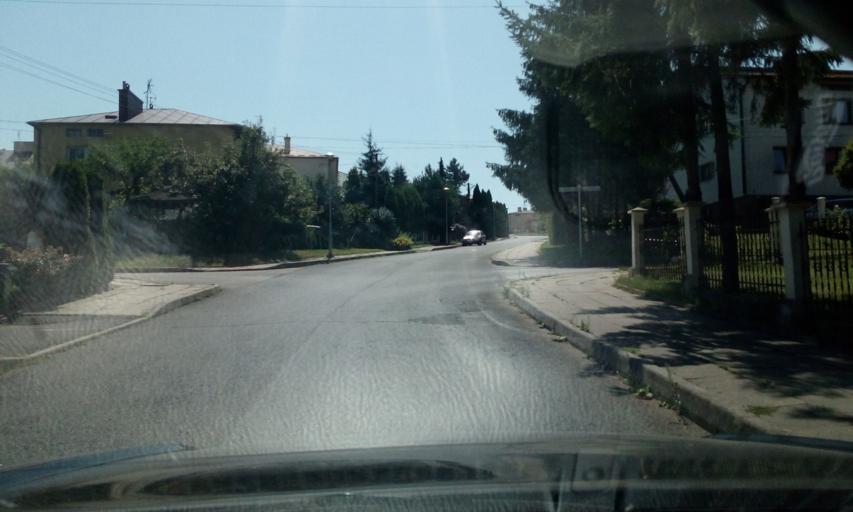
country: PL
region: Subcarpathian Voivodeship
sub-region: Powiat lancucki
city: Lancut
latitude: 50.0579
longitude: 22.2354
